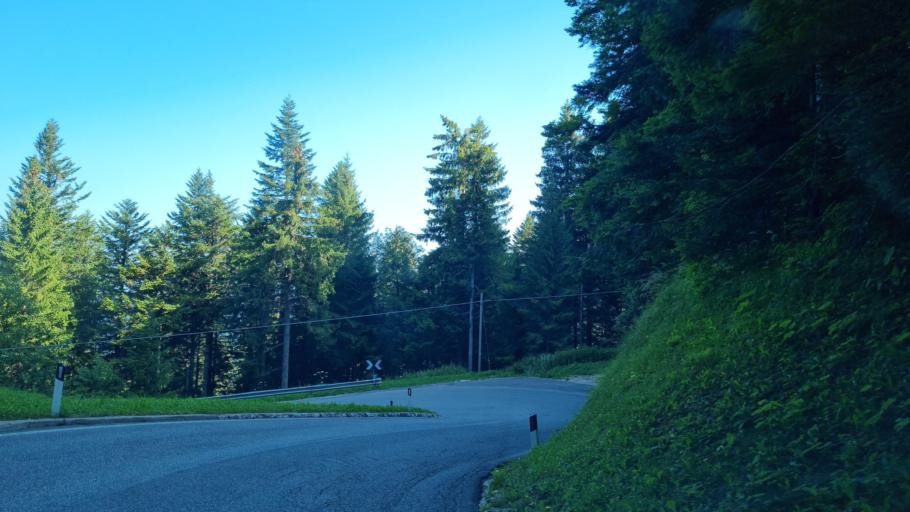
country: IT
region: Trentino-Alto Adige
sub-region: Provincia di Trento
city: Gionghi-Cappella
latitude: 45.9598
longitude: 11.3020
